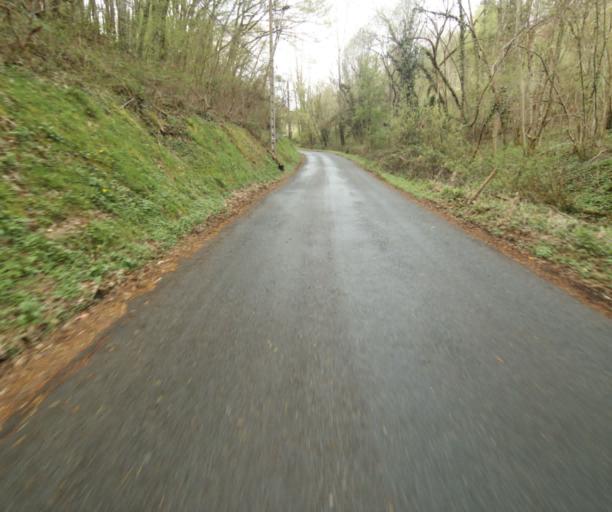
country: FR
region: Limousin
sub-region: Departement de la Correze
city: Tulle
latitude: 45.2625
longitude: 1.7530
